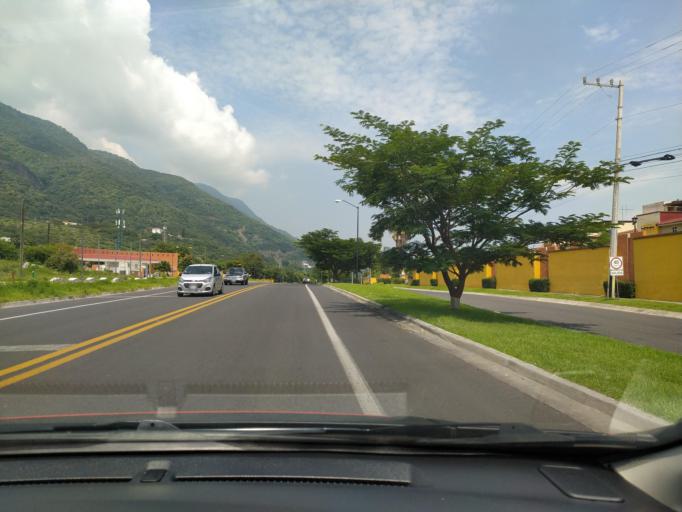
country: MX
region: Jalisco
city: Jocotepec
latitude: 20.2941
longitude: -103.3867
